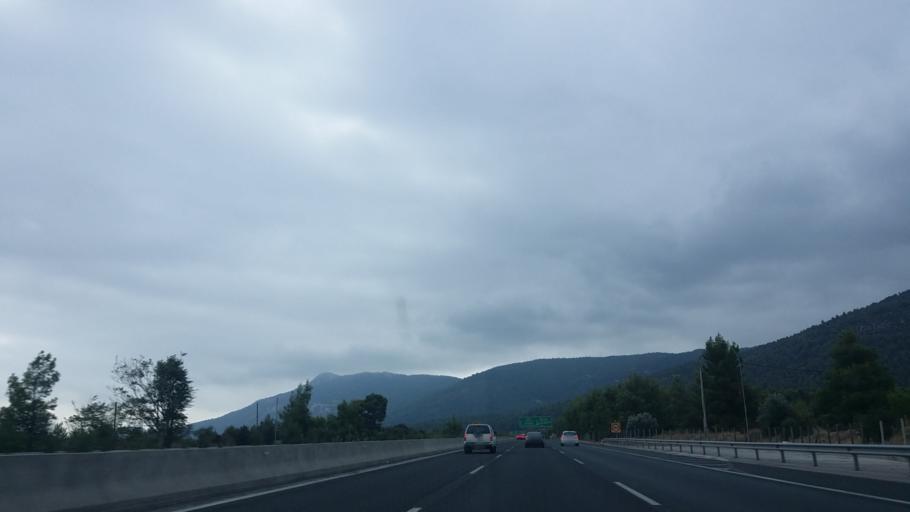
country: GR
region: Attica
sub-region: Nomarchia Anatolikis Attikis
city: Oropos
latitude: 38.2467
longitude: 23.7676
